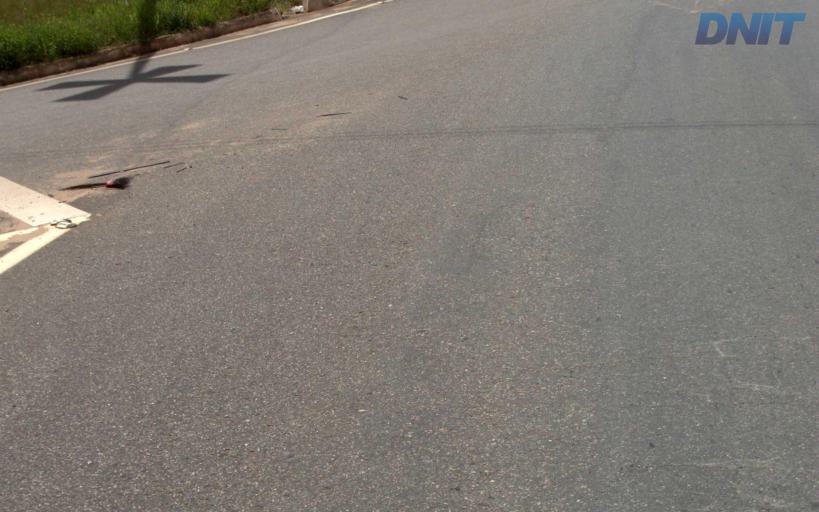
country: BR
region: Minas Gerais
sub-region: Governador Valadares
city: Governador Valadares
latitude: -18.8362
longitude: -41.9633
